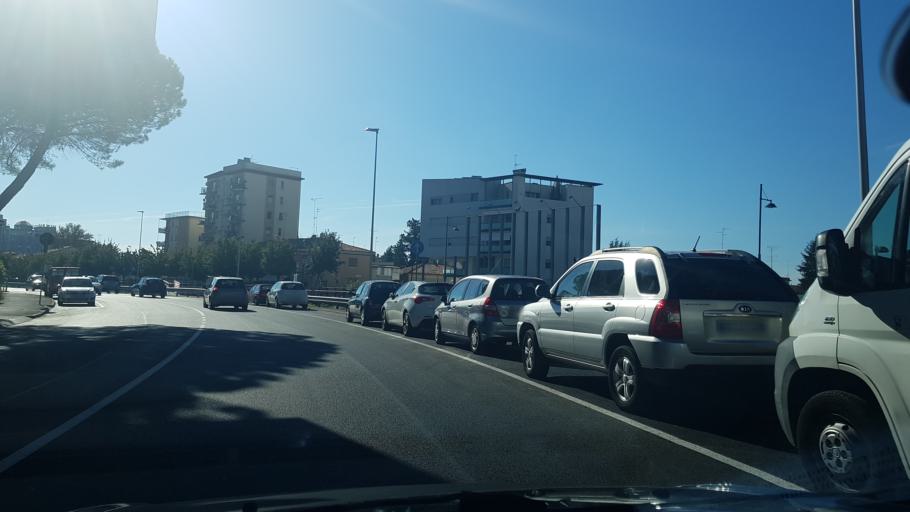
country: IT
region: Friuli Venezia Giulia
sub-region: Provincia di Gorizia
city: Monfalcone
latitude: 45.8087
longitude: 13.5251
